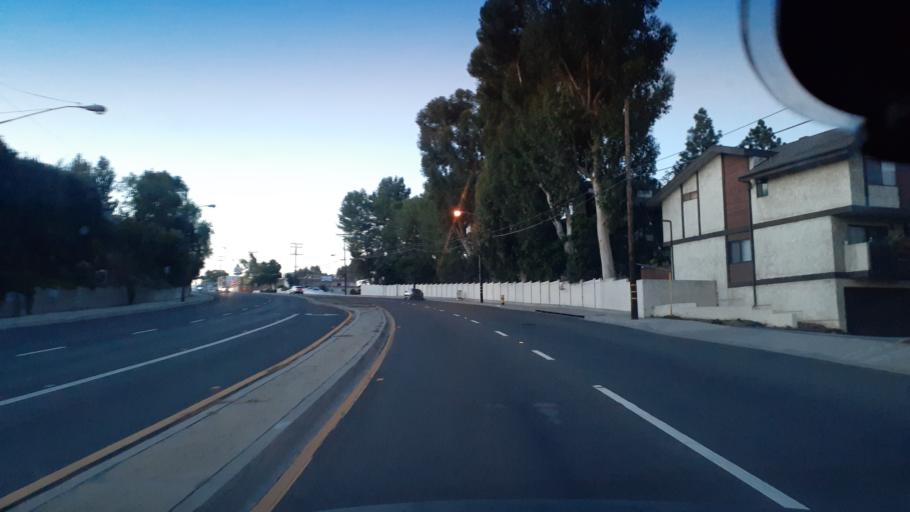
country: US
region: California
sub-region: Los Angeles County
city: Lomita
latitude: 33.7851
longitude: -118.3096
